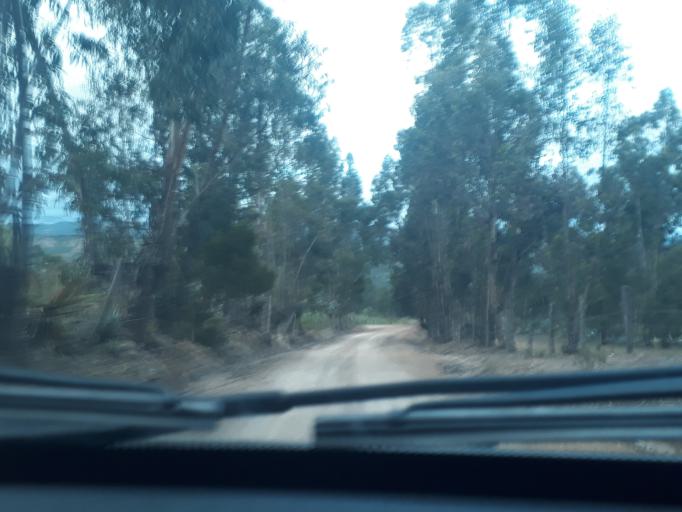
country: CO
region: Boyaca
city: Floresta
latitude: 5.8493
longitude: -72.9503
